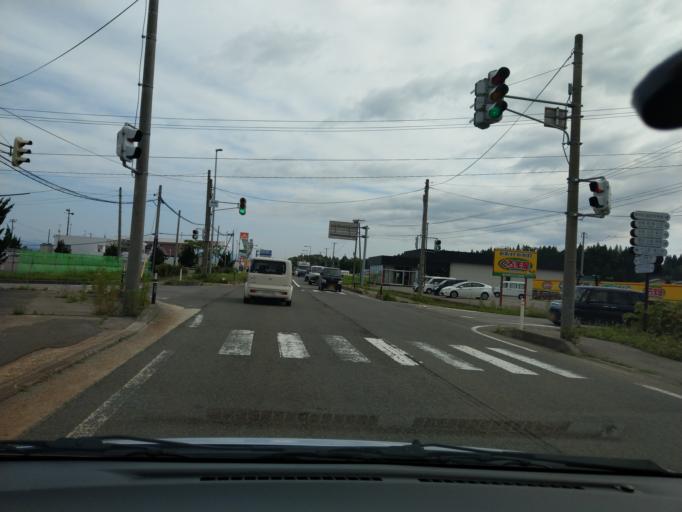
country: JP
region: Akita
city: Yokotemachi
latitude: 39.3773
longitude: 140.5683
